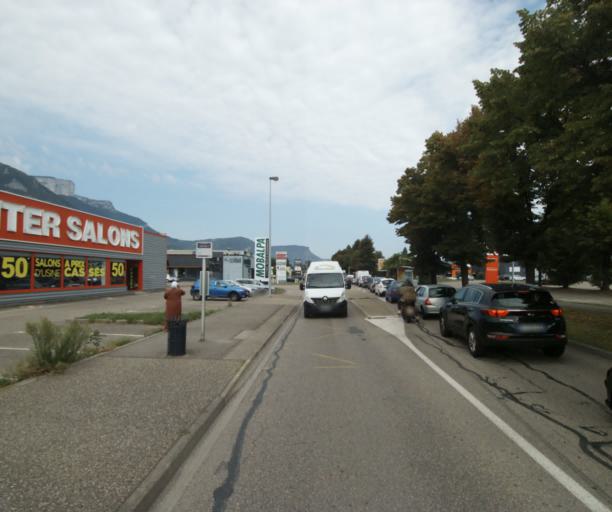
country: FR
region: Rhone-Alpes
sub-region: Departement de l'Isere
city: Saint-Egreve
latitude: 45.2170
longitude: 5.6816
